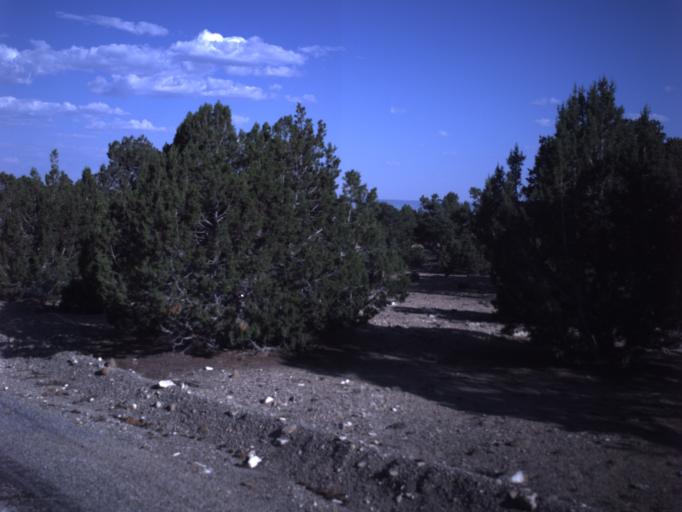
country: US
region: Utah
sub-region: Carbon County
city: Price
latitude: 39.4837
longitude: -110.9176
